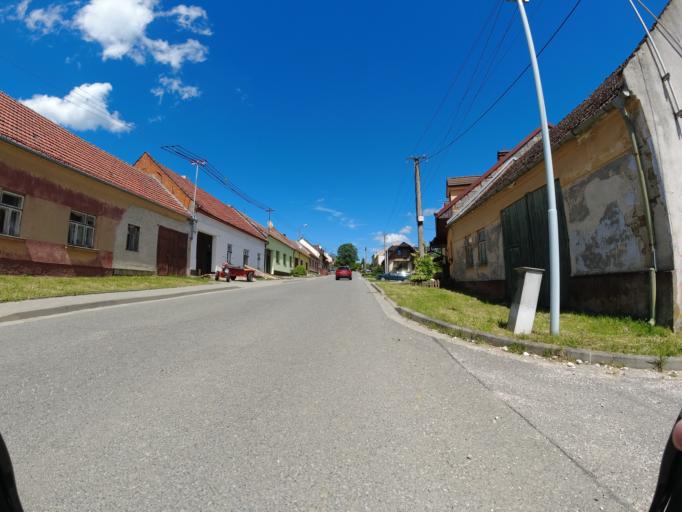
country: CZ
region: Zlin
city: Strani
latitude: 48.9077
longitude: 17.7007
